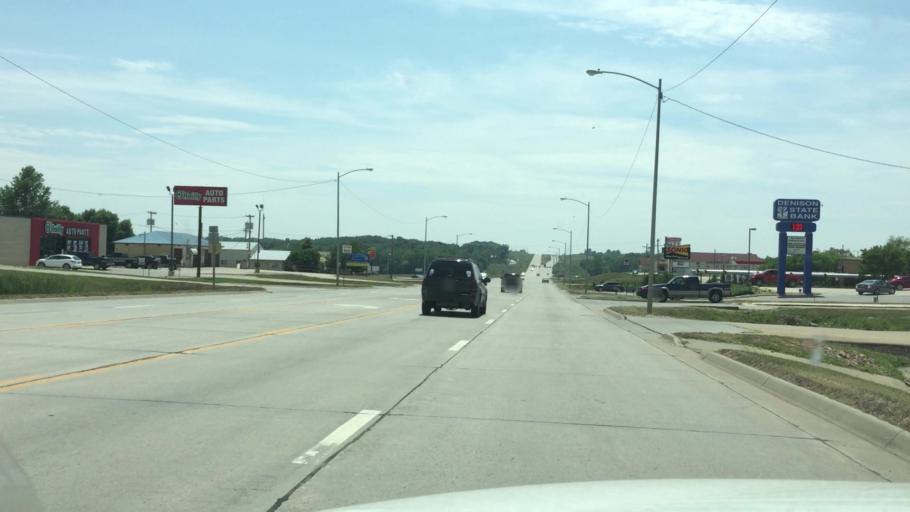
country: US
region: Kansas
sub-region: Jackson County
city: Holton
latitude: 39.4614
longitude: -95.7480
